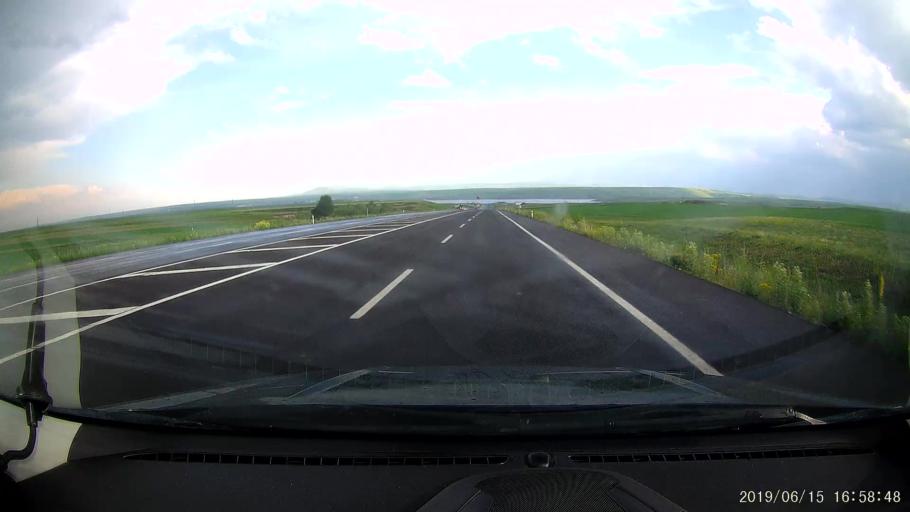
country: TR
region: Kars
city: Susuz
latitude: 40.7600
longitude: 43.1462
